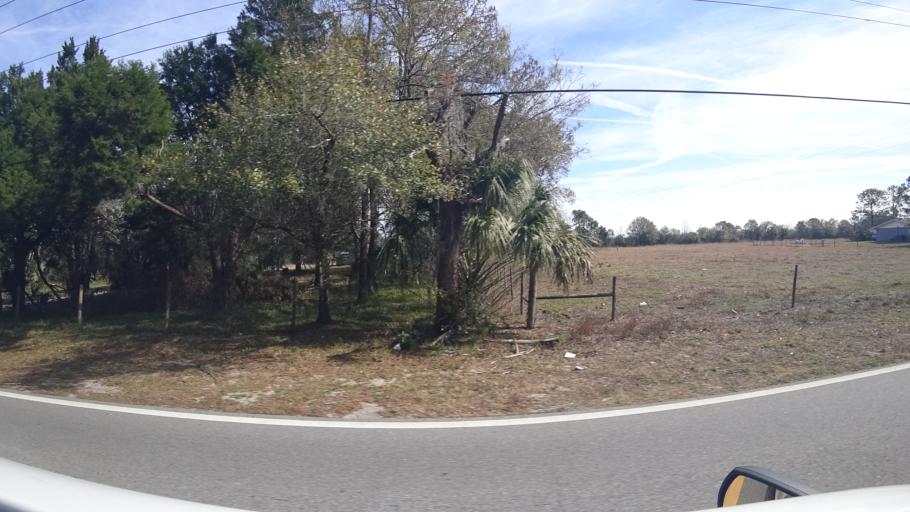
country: US
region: Florida
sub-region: Manatee County
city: Ellenton
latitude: 27.5425
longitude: -82.3694
